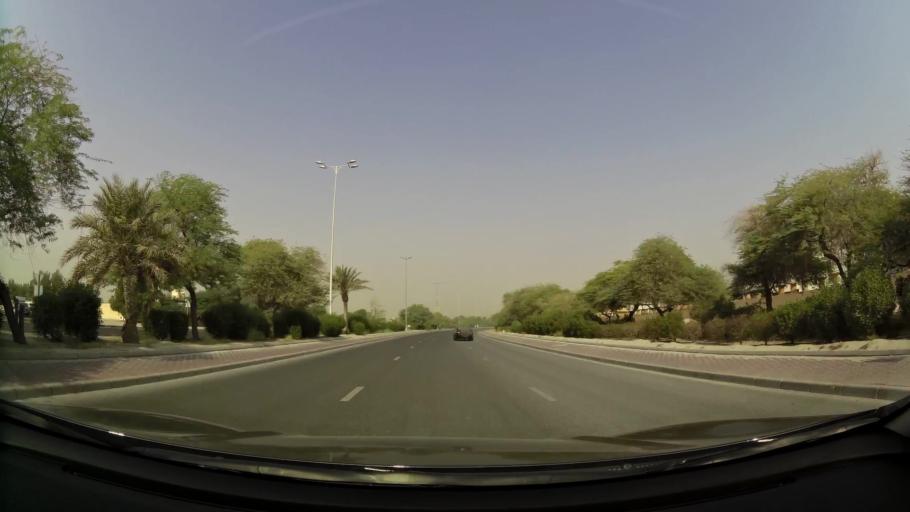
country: KW
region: Al Asimah
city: Ar Rabiyah
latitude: 29.2816
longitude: 47.8354
